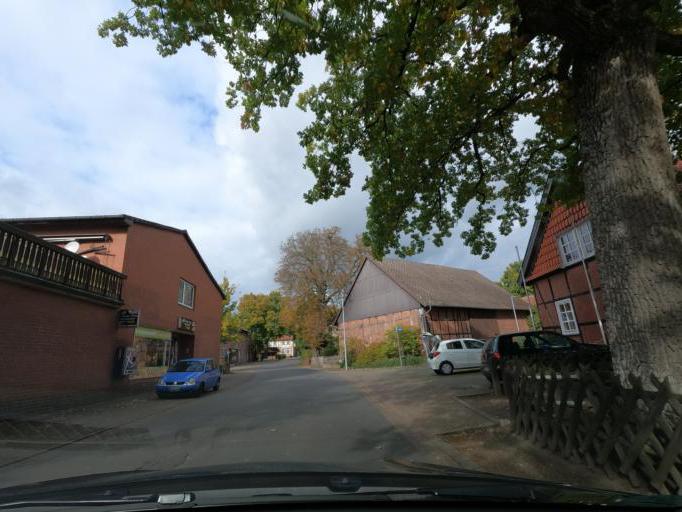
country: DE
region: Lower Saxony
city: Adenbuettel
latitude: 52.3790
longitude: 10.4512
